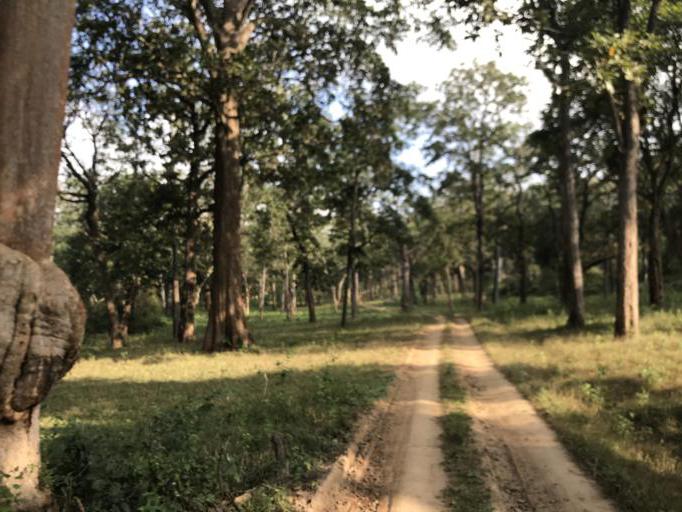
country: IN
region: Karnataka
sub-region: Mysore
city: Heggadadevankote
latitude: 11.9646
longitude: 76.2036
